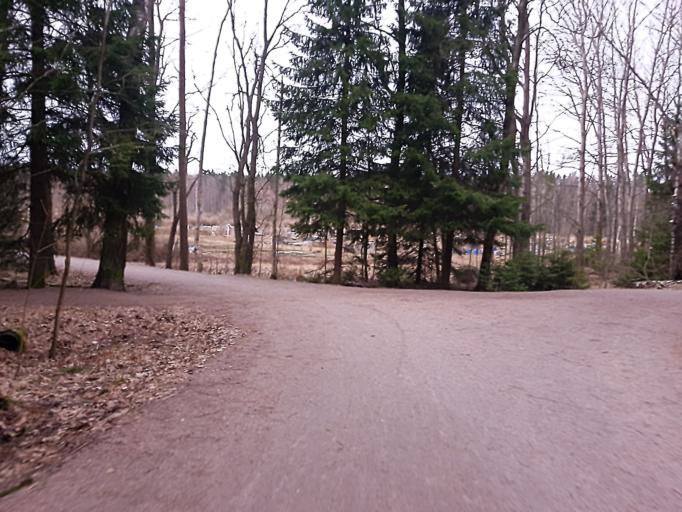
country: FI
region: Uusimaa
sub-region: Helsinki
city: Helsinki
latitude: 60.2457
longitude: 24.9124
